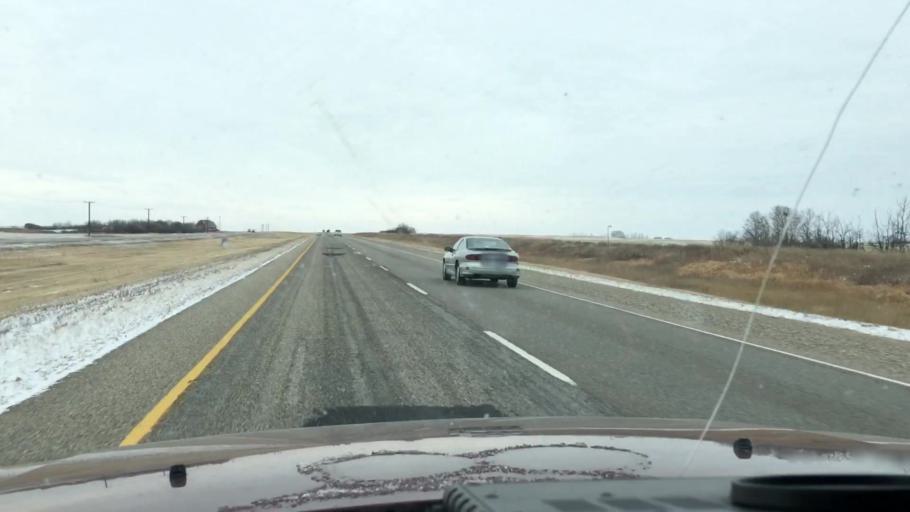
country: CA
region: Saskatchewan
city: Watrous
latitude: 51.4242
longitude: -106.1959
